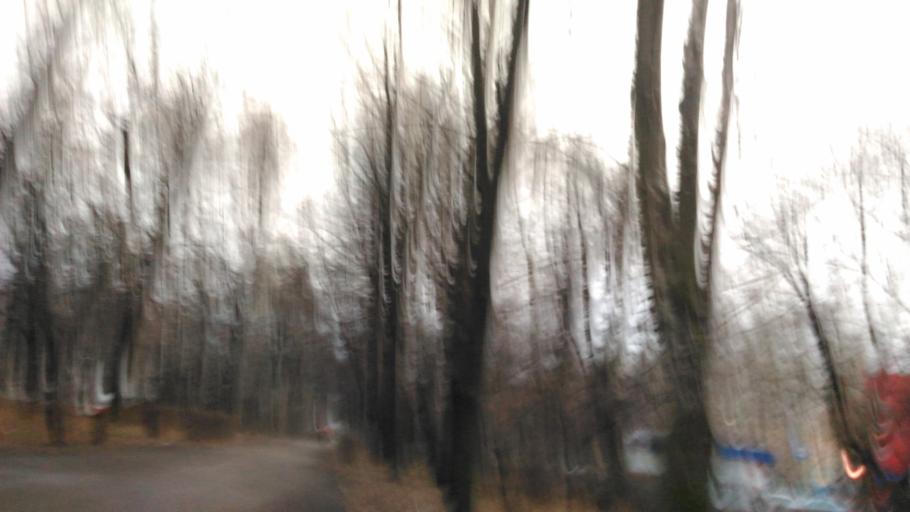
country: RU
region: Ulyanovsk
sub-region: Ulyanovskiy Rayon
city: Ulyanovsk
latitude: 54.3015
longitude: 48.3224
